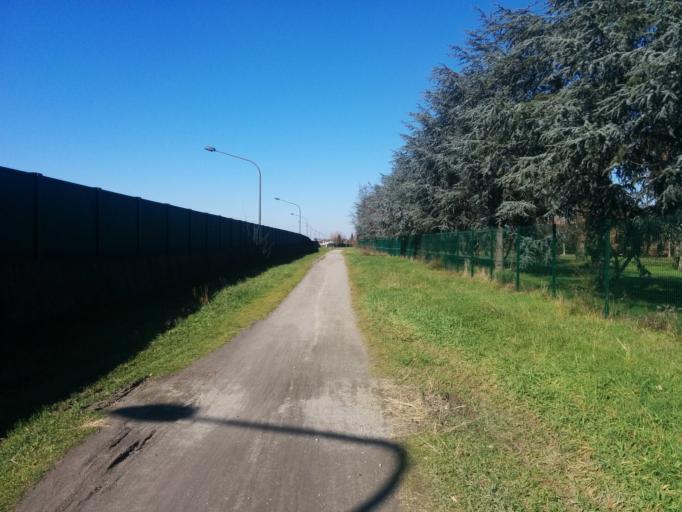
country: FR
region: Midi-Pyrenees
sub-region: Departement de la Haute-Garonne
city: Colomiers
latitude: 43.5816
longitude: 1.3648
